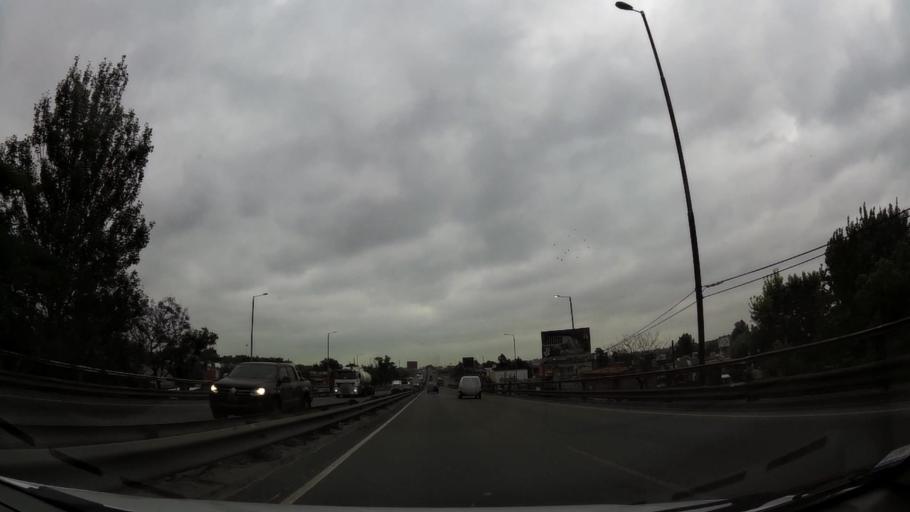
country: AR
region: Buenos Aires
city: San Justo
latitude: -34.7157
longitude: -58.5209
